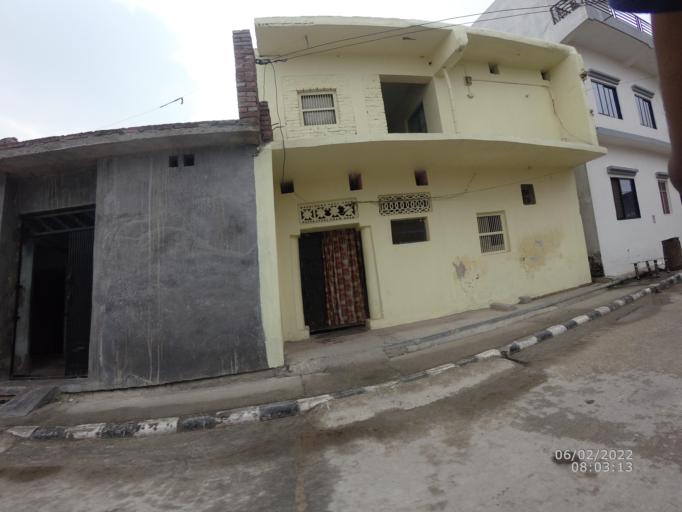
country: NP
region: Western Region
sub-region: Lumbini Zone
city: Bhairahawa
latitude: 27.4792
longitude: 83.4745
